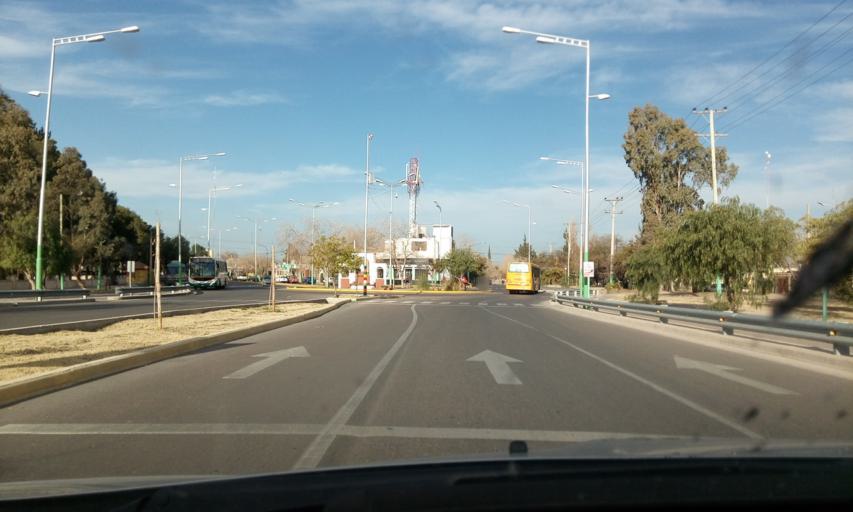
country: AR
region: San Juan
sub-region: Departamento de Rivadavia
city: Rivadavia
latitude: -31.5309
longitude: -68.5981
